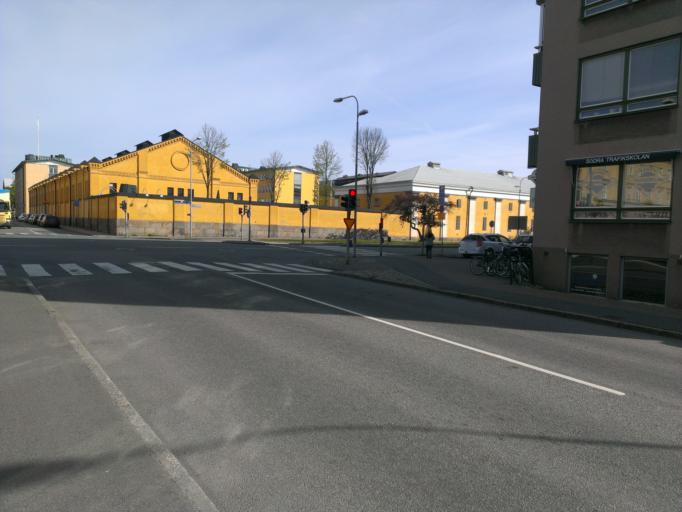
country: SE
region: Skane
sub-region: Kristianstads Kommun
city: Kristianstad
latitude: 56.0258
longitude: 14.1592
